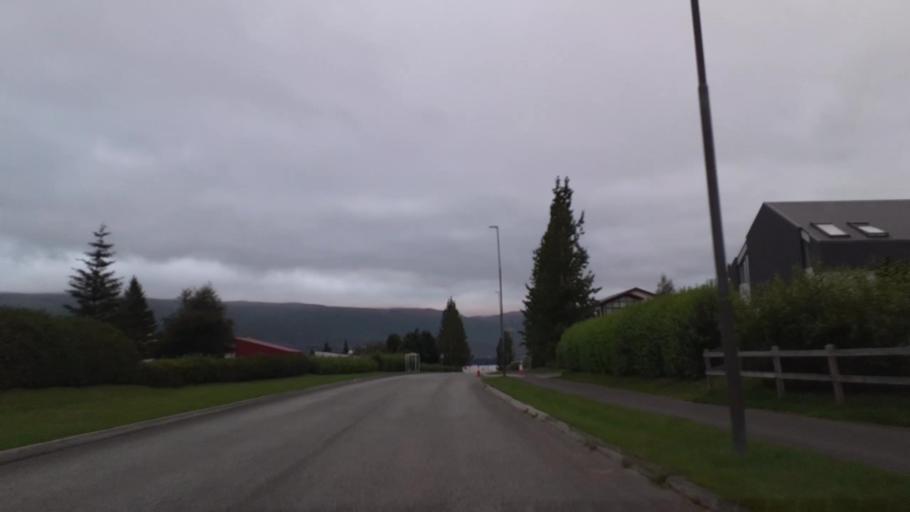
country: IS
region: Northeast
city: Akureyri
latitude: 65.6955
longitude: -18.1388
